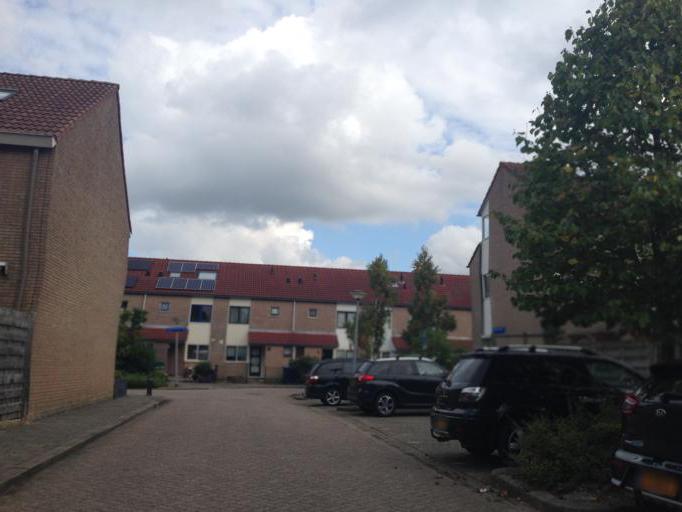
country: NL
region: Flevoland
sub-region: Gemeente Almere
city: Almere Stad
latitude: 52.3996
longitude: 5.2724
